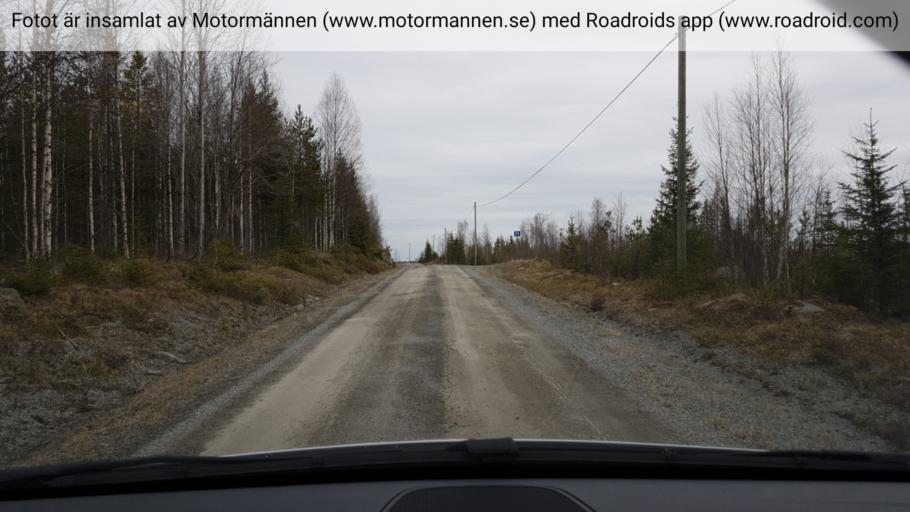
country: SE
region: Jaemtland
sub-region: Bergs Kommun
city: Hoverberg
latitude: 62.8443
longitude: 14.5694
